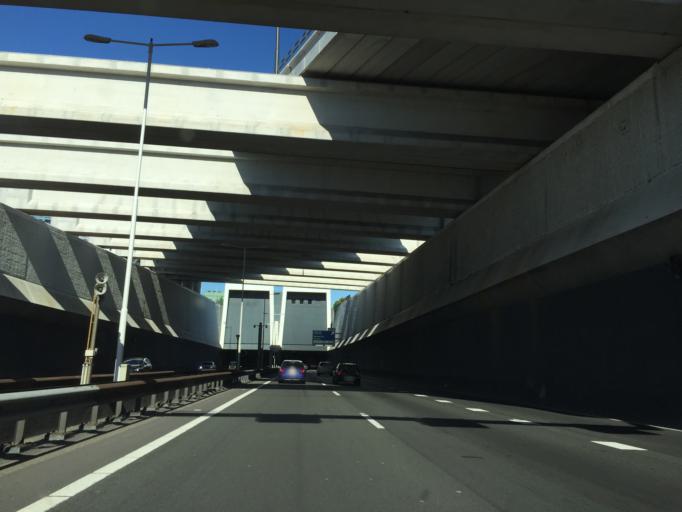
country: NL
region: South Holland
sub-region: Gemeente Spijkenisse
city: Spijkenisse
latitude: 51.8700
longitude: 4.3248
